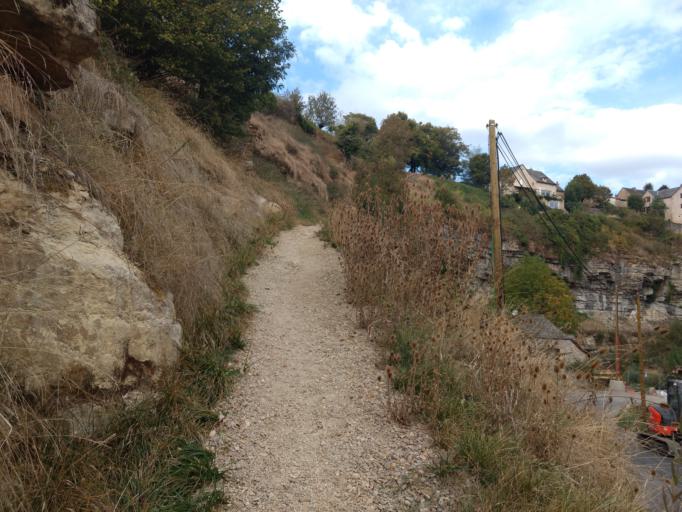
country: FR
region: Midi-Pyrenees
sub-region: Departement de l'Aveyron
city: Bozouls
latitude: 44.4674
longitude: 2.7170
